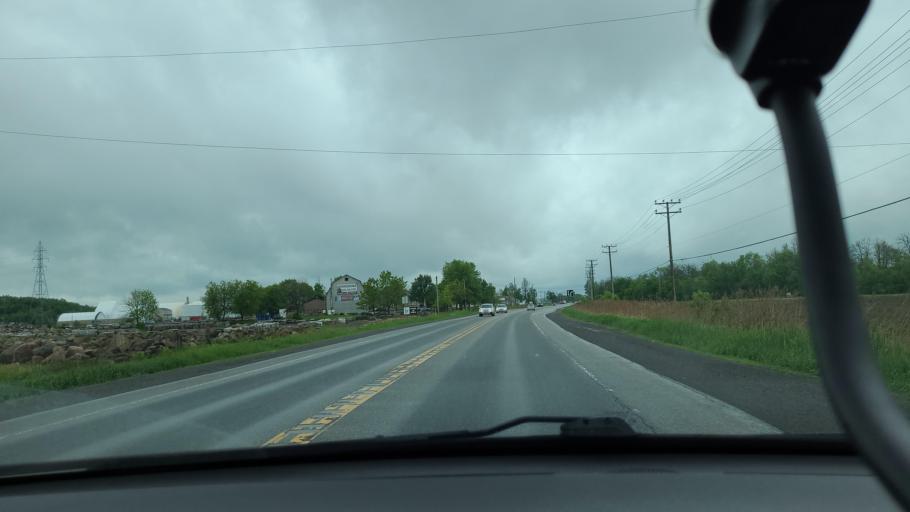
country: CA
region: Quebec
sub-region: Laurentides
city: Saint-Jerome
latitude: 45.7358
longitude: -74.0415
